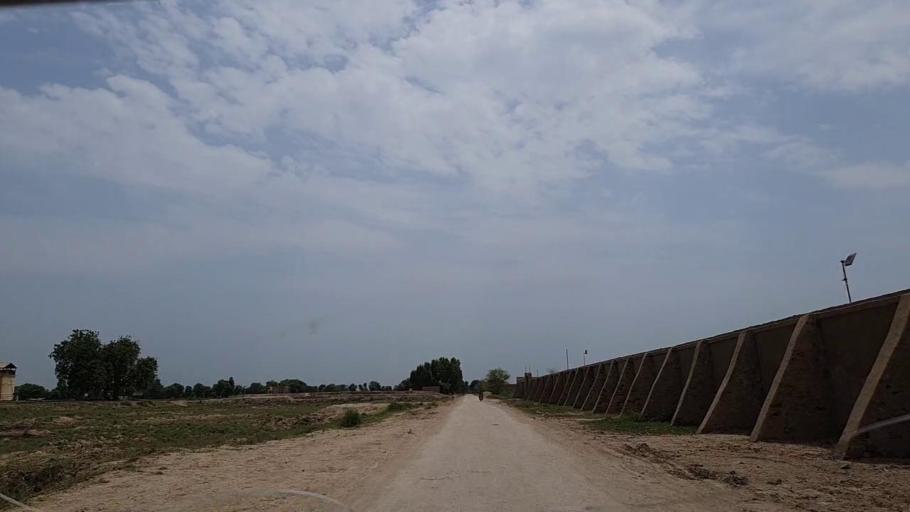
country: PK
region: Sindh
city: Tharu Shah
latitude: 26.9347
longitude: 68.1069
